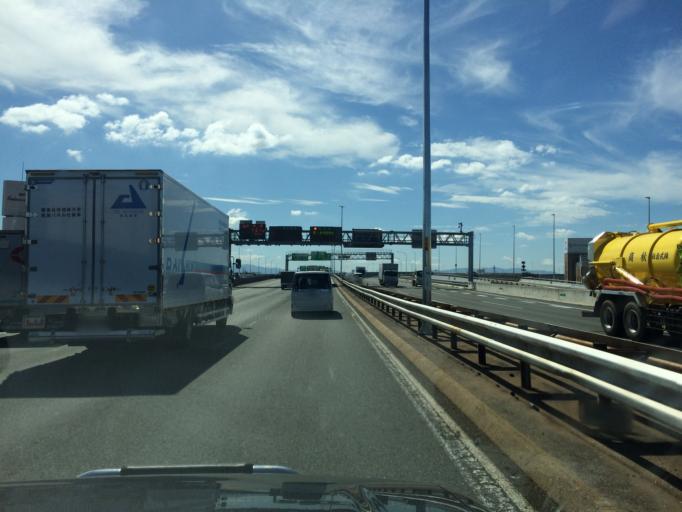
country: JP
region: Osaka
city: Yao
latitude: 34.5960
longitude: 135.5748
